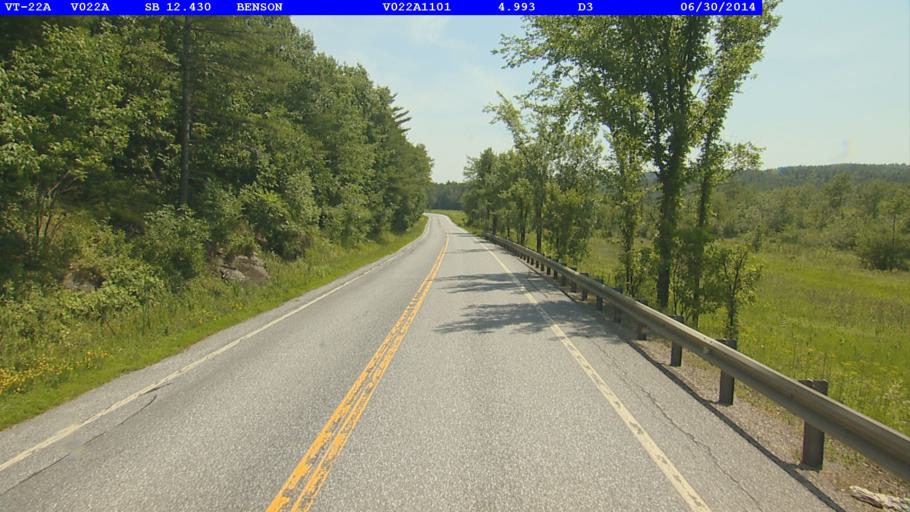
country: US
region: Vermont
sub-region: Rutland County
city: Fair Haven
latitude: 43.7394
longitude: -73.3067
